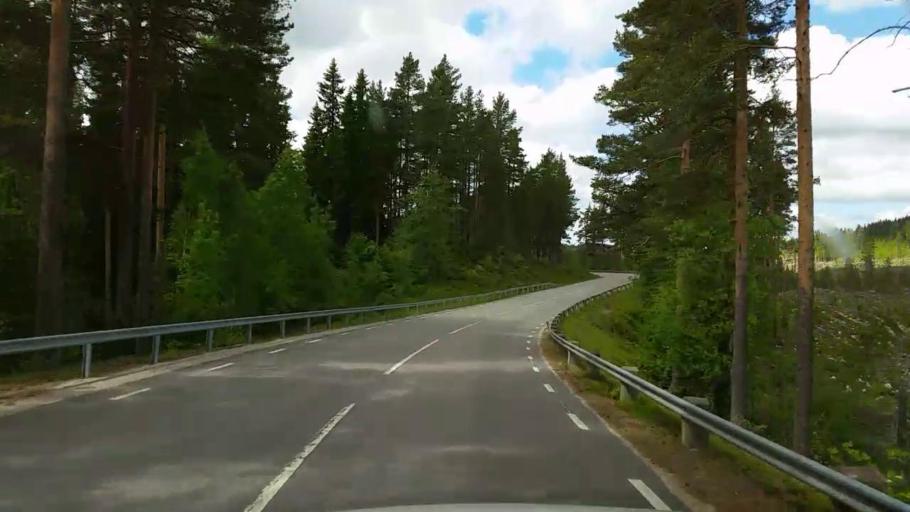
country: SE
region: Gaevleborg
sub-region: Bollnas Kommun
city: Vittsjo
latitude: 61.1448
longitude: 16.1665
